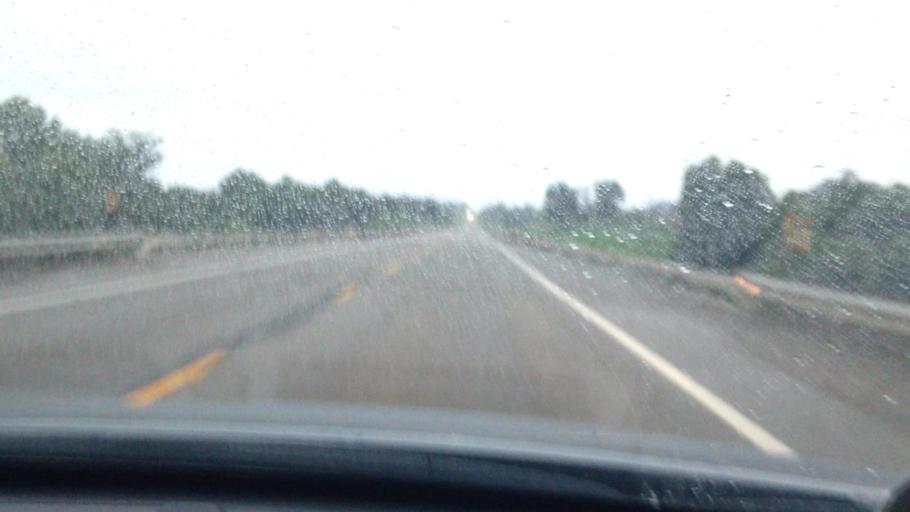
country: US
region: Kansas
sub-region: Brown County
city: Hiawatha
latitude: 39.8330
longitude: -95.5270
